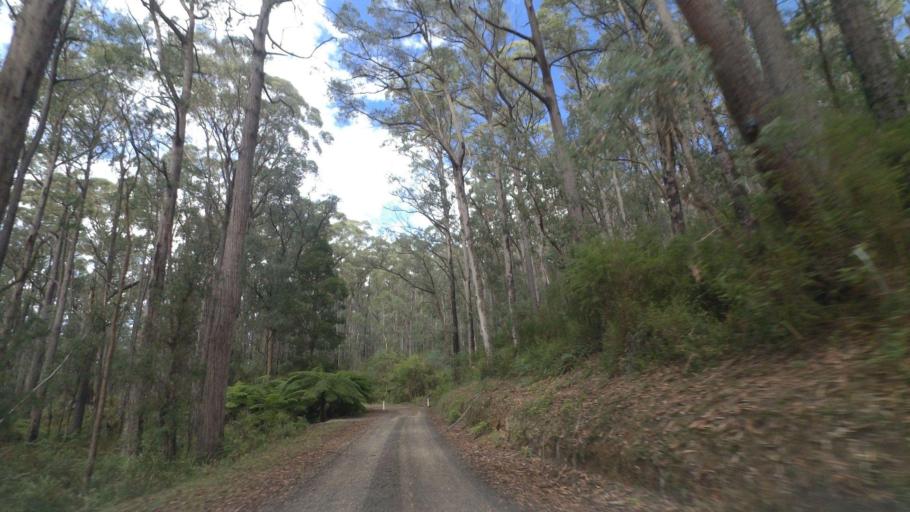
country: AU
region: Victoria
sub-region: Cardinia
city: Gembrook
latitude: -37.9114
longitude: 145.6232
